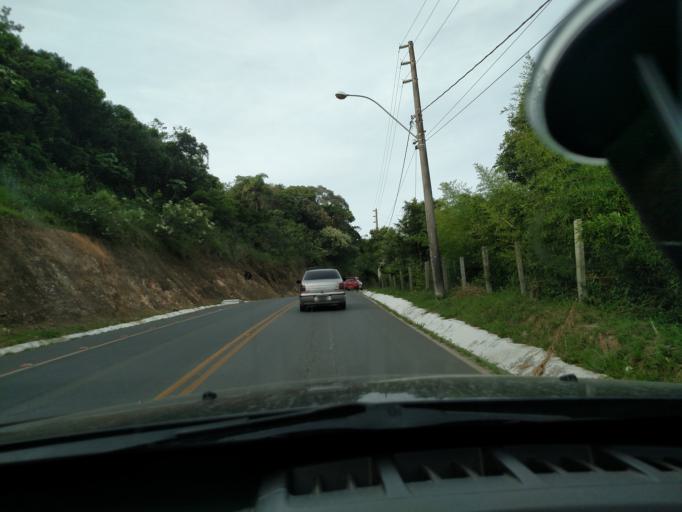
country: BR
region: Santa Catarina
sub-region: Porto Belo
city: Porto Belo
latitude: -27.1585
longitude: -48.4915
